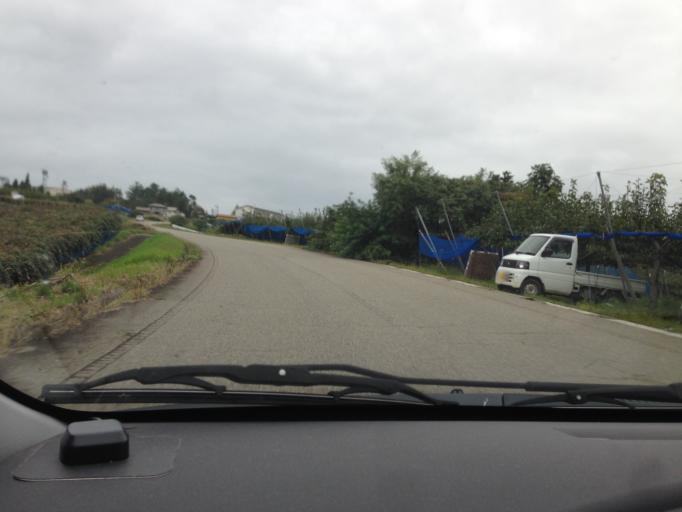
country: JP
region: Fukushima
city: Kitakata
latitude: 37.5040
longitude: 139.8158
